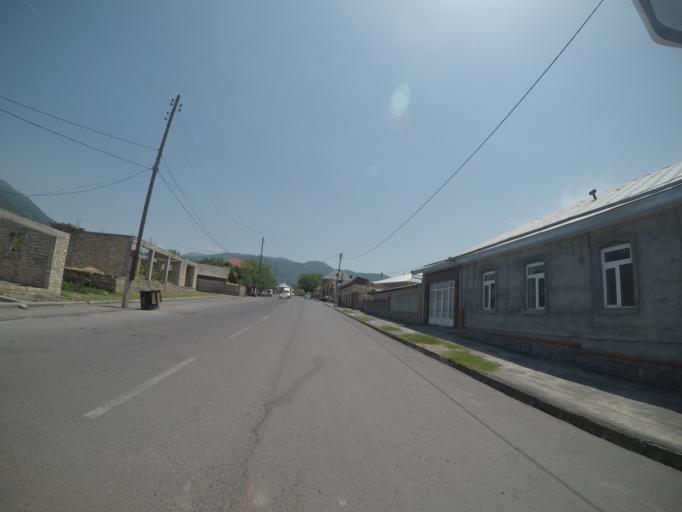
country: AZ
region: Qakh Rayon
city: Qax
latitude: 41.4146
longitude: 46.9106
